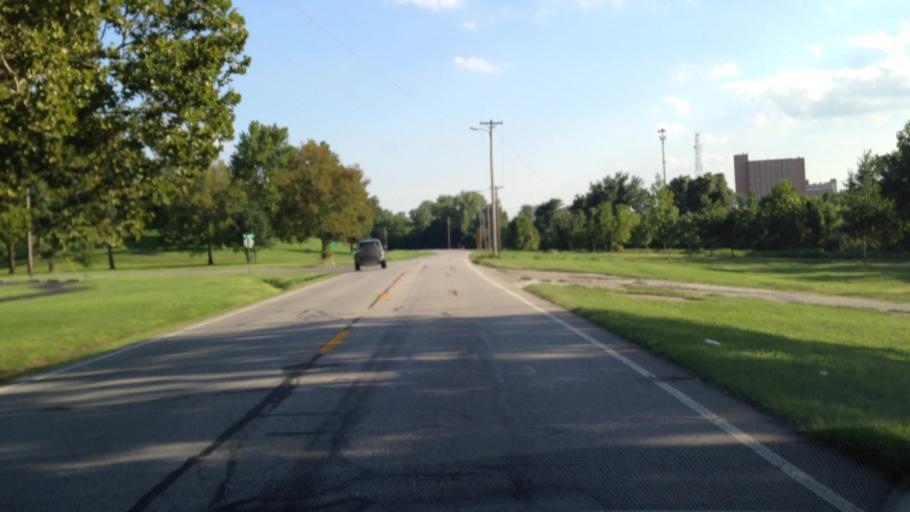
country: US
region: Missouri
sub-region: Jasper County
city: Joplin
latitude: 37.0962
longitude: -94.5109
